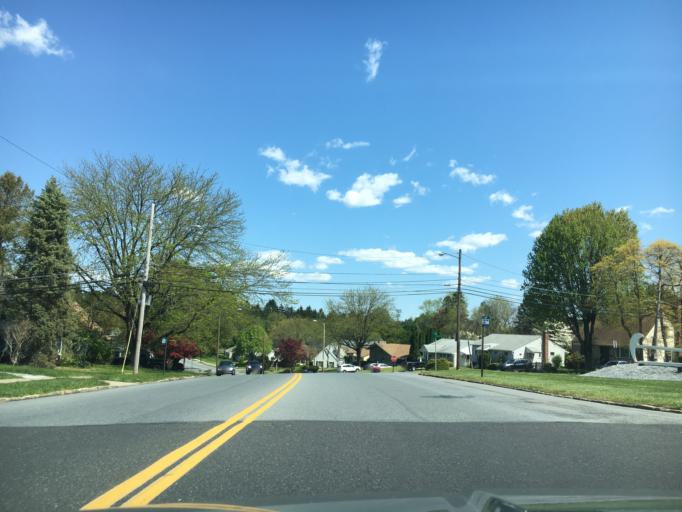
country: US
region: Pennsylvania
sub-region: Lehigh County
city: Allentown
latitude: 40.5829
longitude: -75.4790
